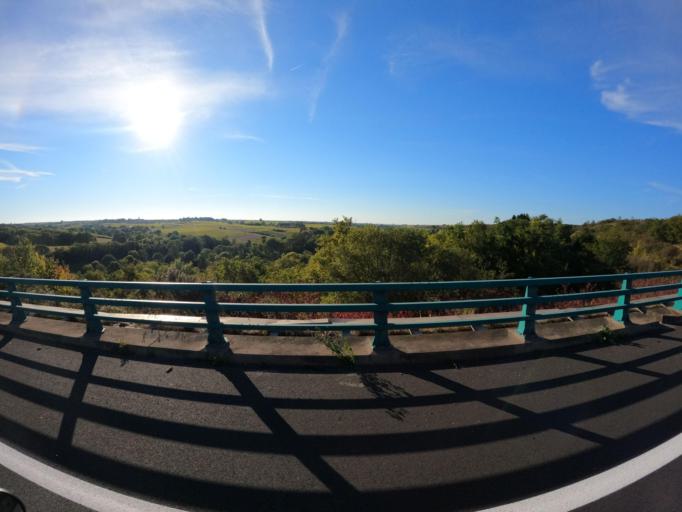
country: FR
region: Pays de la Loire
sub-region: Departement de Maine-et-Loire
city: Beaulieu-sur-Layon
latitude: 47.3122
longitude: -0.6069
